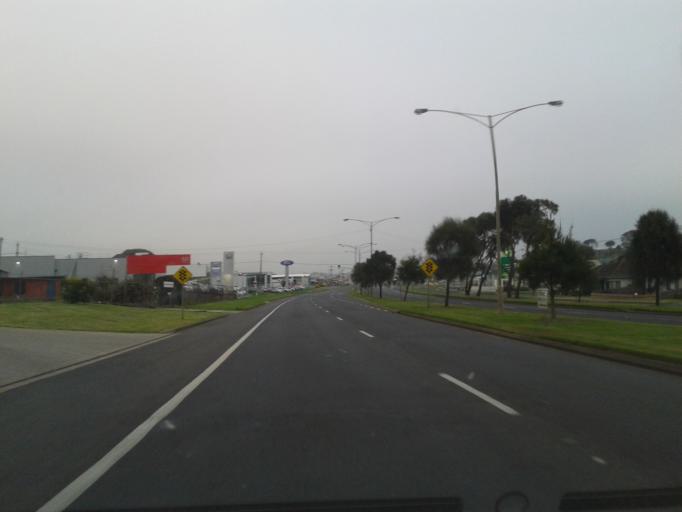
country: AU
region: Victoria
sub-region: Warrnambool
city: Warrnambool
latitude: -38.3705
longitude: 142.4703
